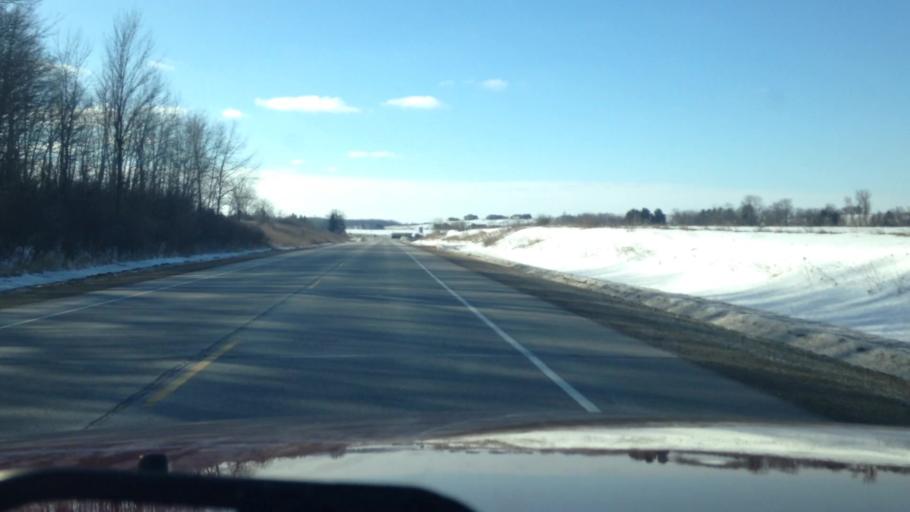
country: US
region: Wisconsin
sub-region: Waukesha County
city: Oconomowoc
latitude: 43.1843
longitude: -88.5087
